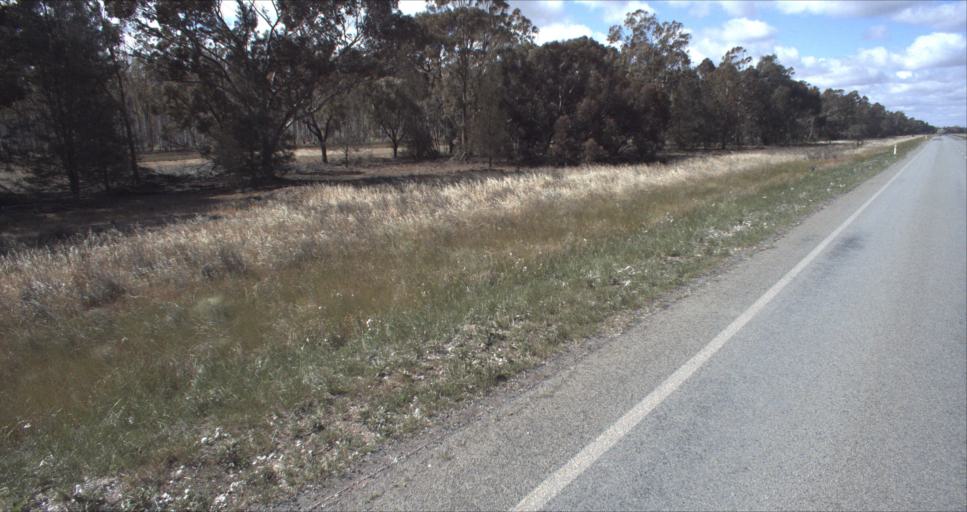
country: AU
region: New South Wales
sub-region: Murrumbidgee Shire
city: Darlington Point
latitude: -34.5812
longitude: 146.1650
